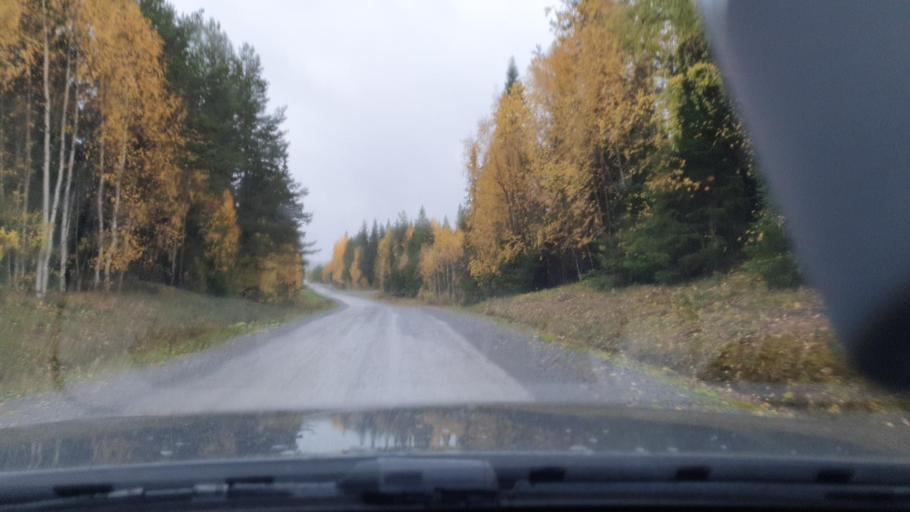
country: SE
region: Jaemtland
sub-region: Stroemsunds Kommun
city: Stroemsund
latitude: 63.5435
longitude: 15.5662
